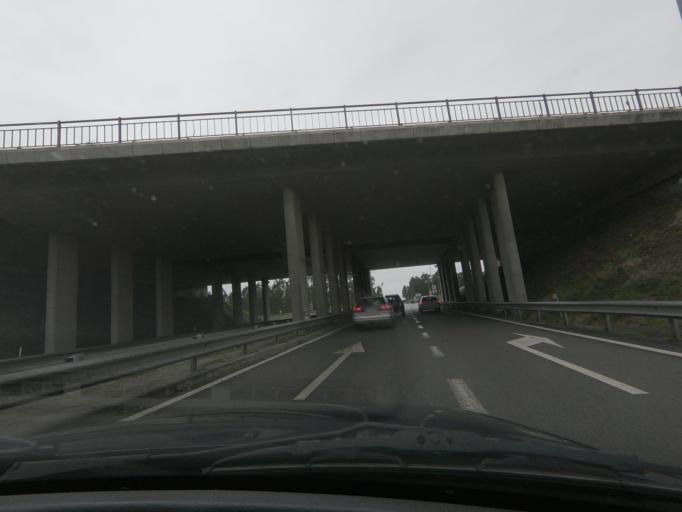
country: PT
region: Porto
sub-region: Vila do Conde
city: Arvore
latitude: 41.3012
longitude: -8.6999
